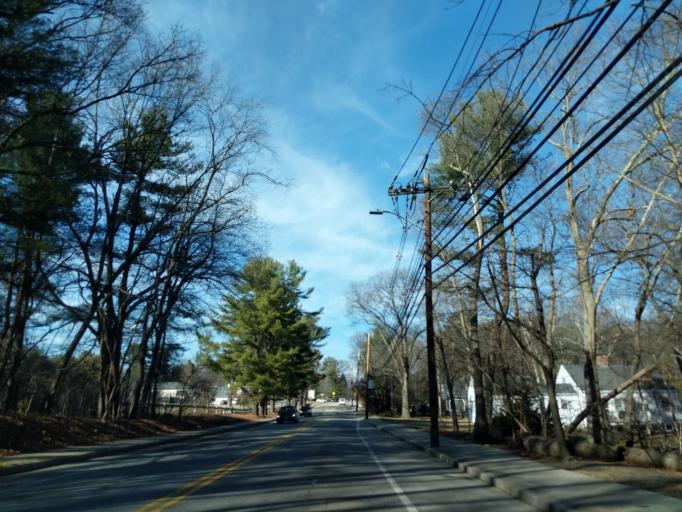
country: US
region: Massachusetts
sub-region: Middlesex County
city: Natick
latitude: 42.2905
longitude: -71.3761
